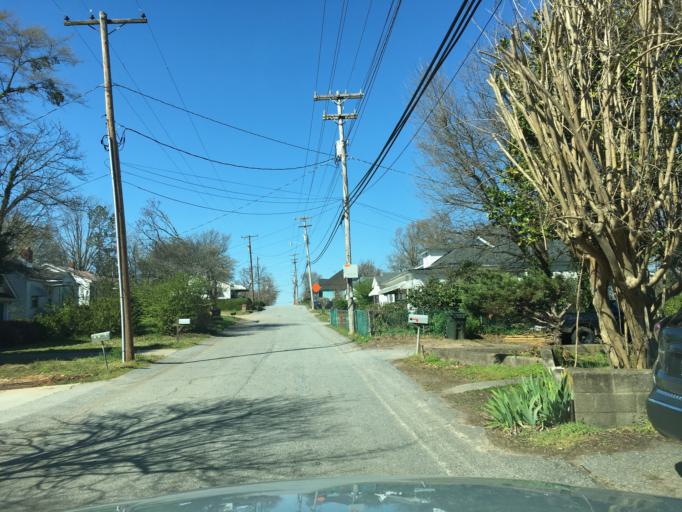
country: US
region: South Carolina
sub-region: Greenville County
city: Greer
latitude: 34.9437
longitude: -82.2380
